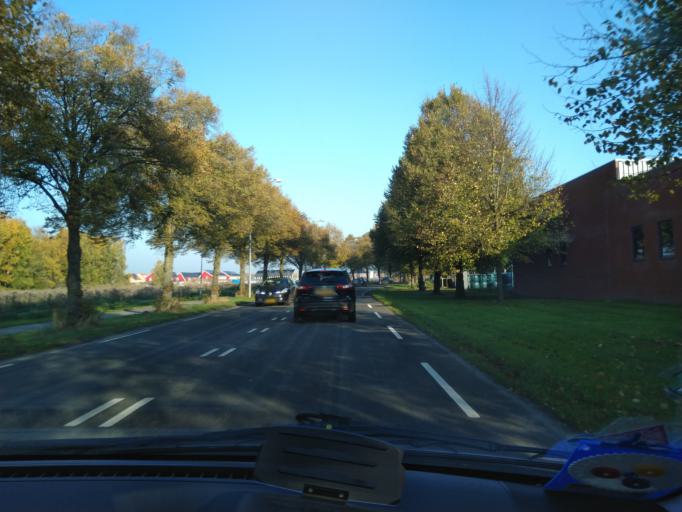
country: NL
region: Groningen
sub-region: Gemeente Hoogezand-Sappemeer
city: Hoogezand
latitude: 53.1540
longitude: 6.7726
